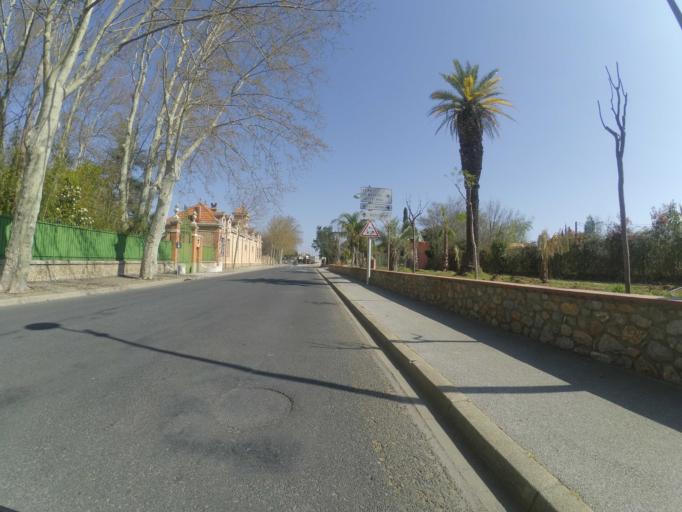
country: FR
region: Languedoc-Roussillon
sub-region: Departement des Pyrenees-Orientales
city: Thuir
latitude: 42.6370
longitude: 2.7604
